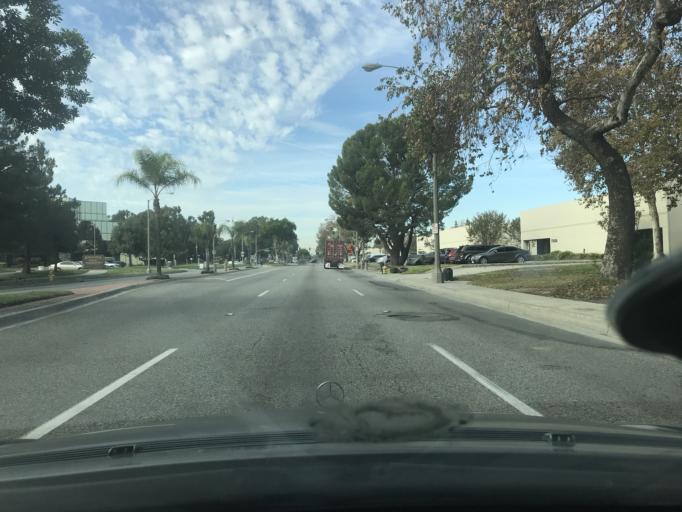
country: US
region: California
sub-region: Los Angeles County
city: Santa Fe Springs
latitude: 33.9443
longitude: -118.0786
